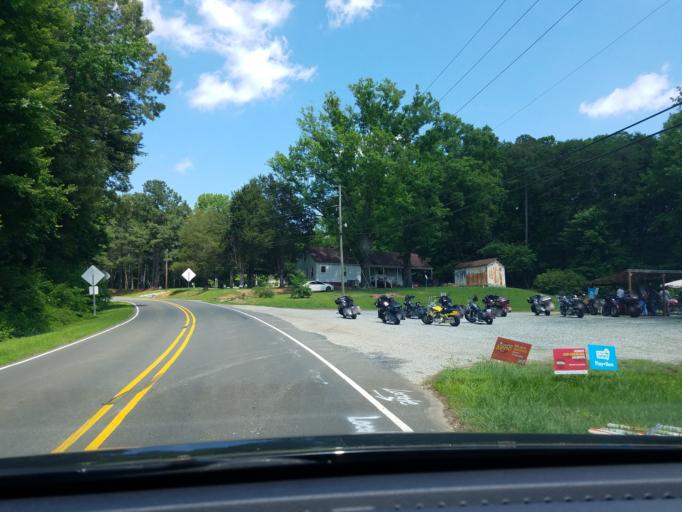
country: US
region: North Carolina
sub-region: Granville County
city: Butner
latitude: 36.1727
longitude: -78.8566
